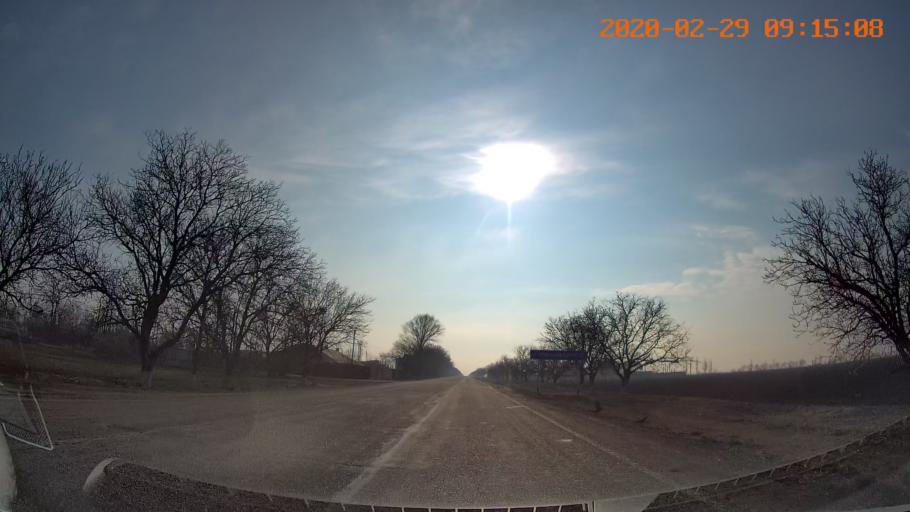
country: MD
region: Telenesti
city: Pervomaisc
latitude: 46.8031
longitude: 29.8639
